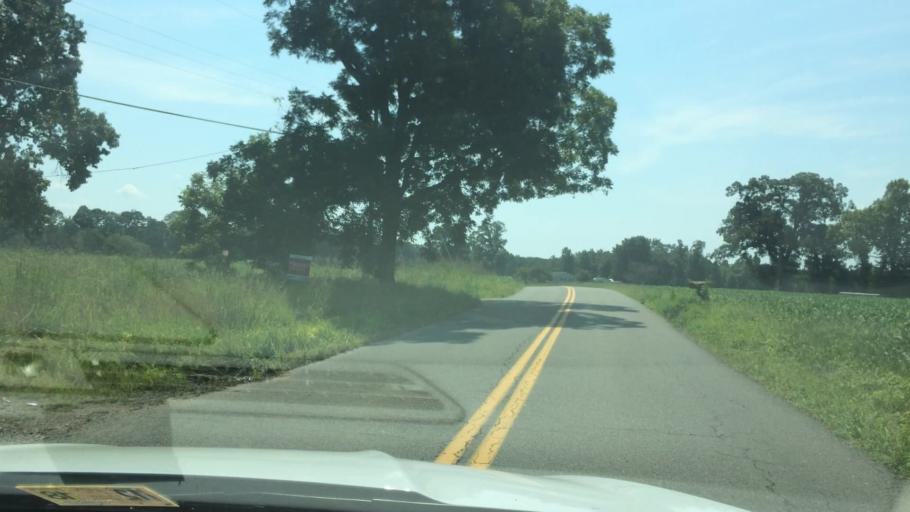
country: US
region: Virginia
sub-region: Henrico County
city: Sandston
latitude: 37.5084
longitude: -77.1595
